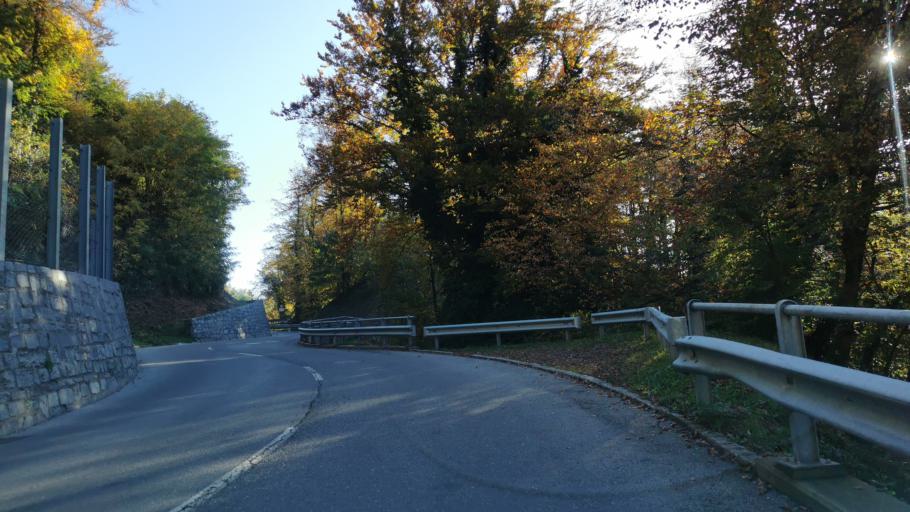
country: CH
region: Ticino
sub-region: Lugano District
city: Pura
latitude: 46.0225
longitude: 8.8535
